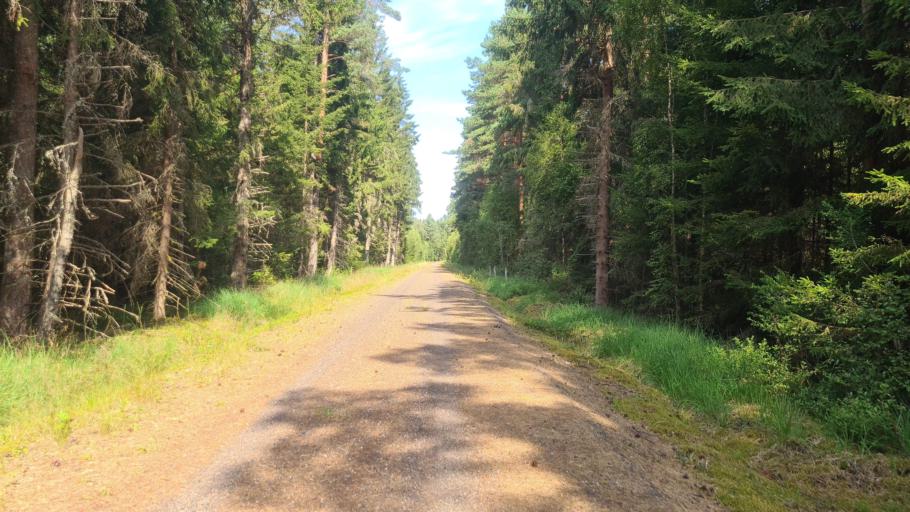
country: SE
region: Kronoberg
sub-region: Ljungby Kommun
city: Lagan
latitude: 56.9536
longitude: 13.9598
